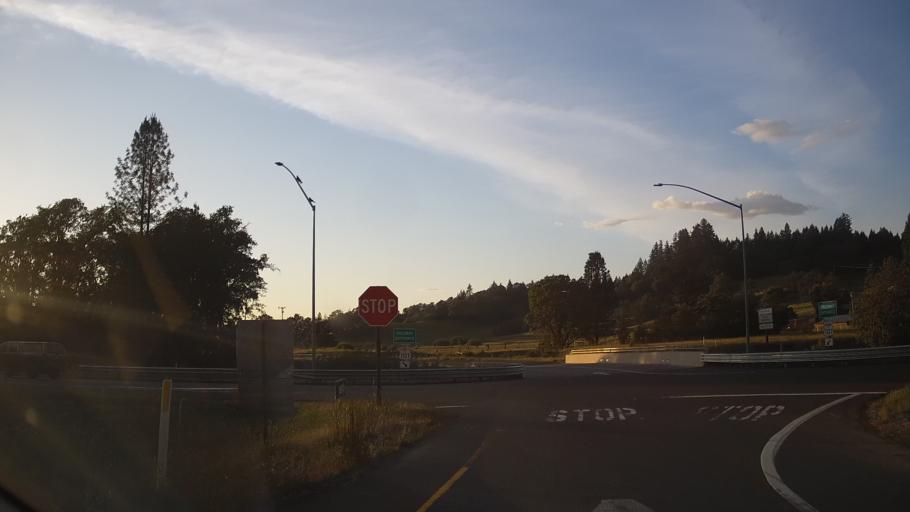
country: US
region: California
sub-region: Mendocino County
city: Willits
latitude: 39.3752
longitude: -123.3244
